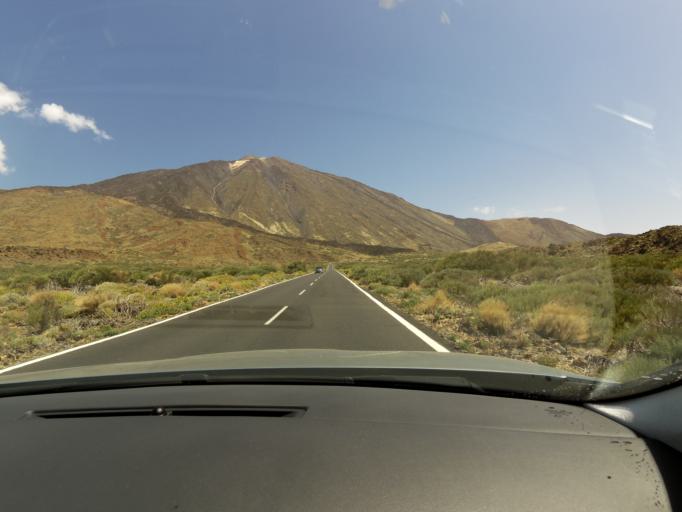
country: ES
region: Canary Islands
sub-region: Provincia de Santa Cruz de Tenerife
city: Vilaflor
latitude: 28.2366
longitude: -16.6296
